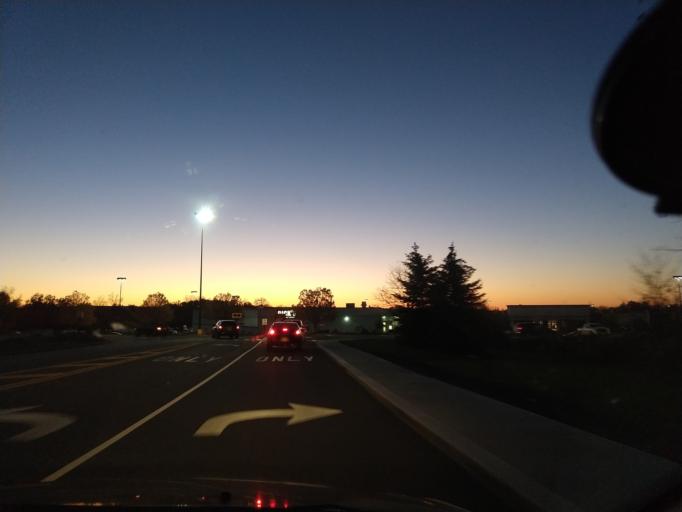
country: US
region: New York
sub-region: Tompkins County
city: Lansing
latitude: 42.4824
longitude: -76.4879
